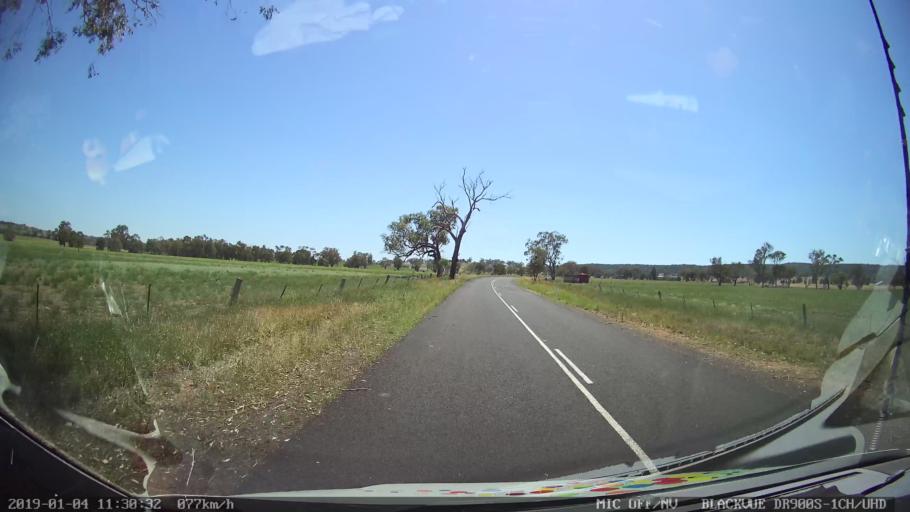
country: AU
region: New South Wales
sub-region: Cabonne
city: Molong
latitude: -33.0770
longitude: 148.7821
